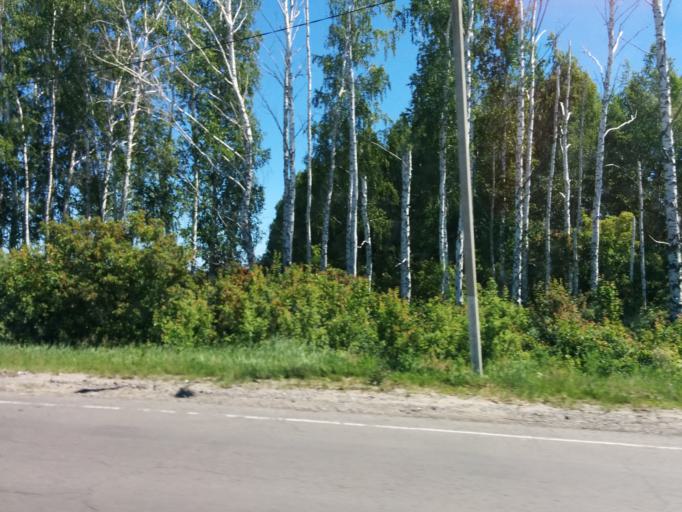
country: RU
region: Tambov
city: Goreloye
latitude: 53.1128
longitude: 41.5352
